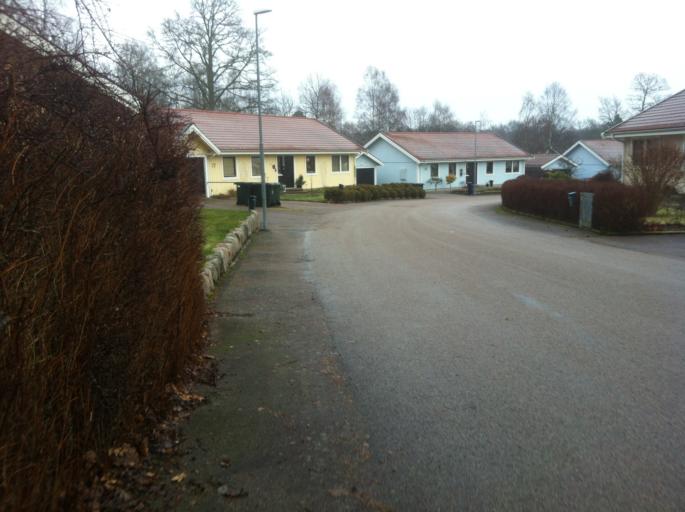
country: SE
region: Skane
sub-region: Perstorps Kommun
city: Perstorp
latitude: 56.1464
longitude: 13.3759
